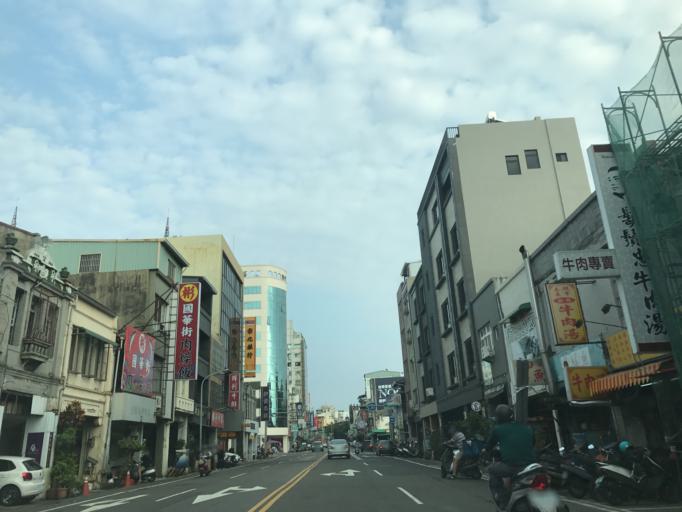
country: TW
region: Taiwan
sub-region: Tainan
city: Tainan
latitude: 22.9985
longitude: 120.1968
